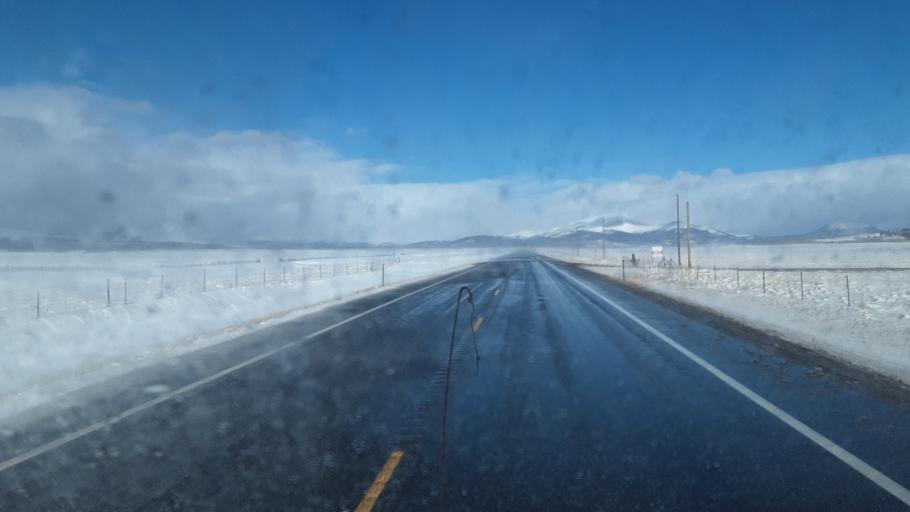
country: US
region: Colorado
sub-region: Park County
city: Fairplay
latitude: 39.1578
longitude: -105.9999
